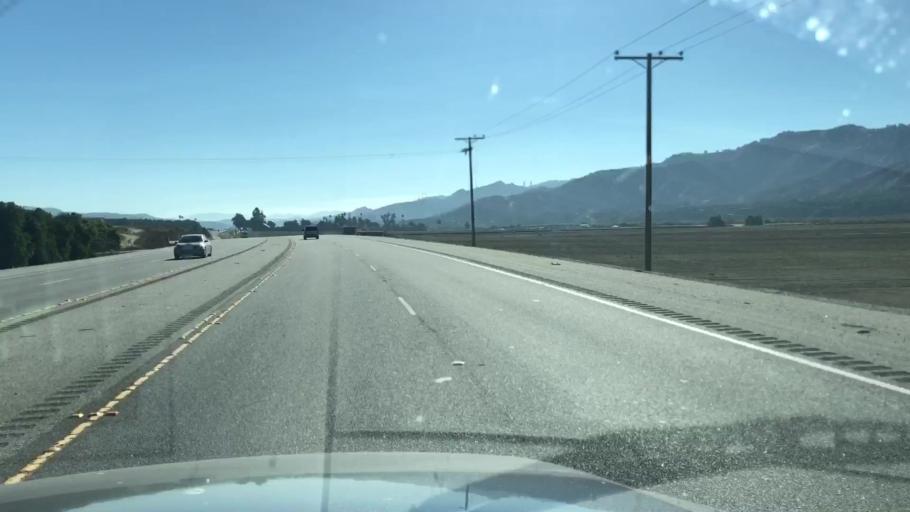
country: US
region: California
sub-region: Ventura County
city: Piru
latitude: 34.4077
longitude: -118.7716
